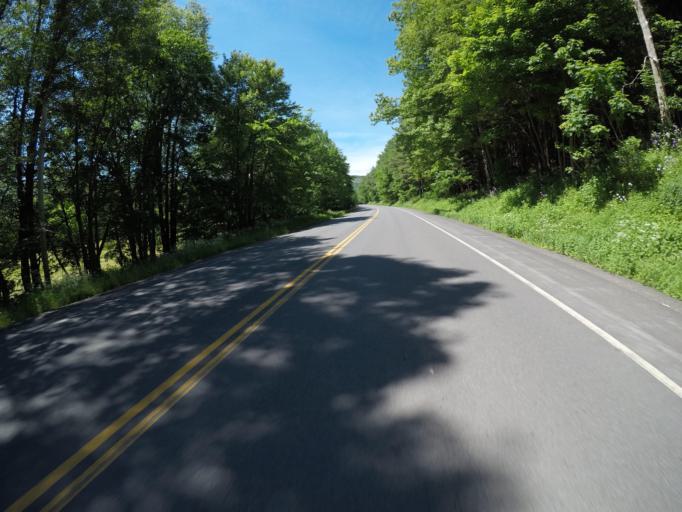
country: US
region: New York
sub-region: Delaware County
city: Delhi
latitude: 42.2627
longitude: -74.9297
